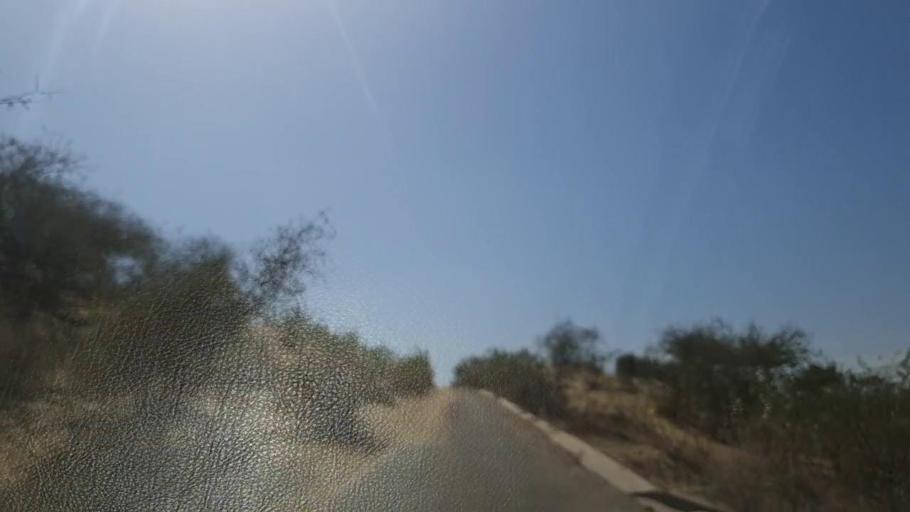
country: PK
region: Sindh
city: Naukot
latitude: 24.8351
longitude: 69.5943
